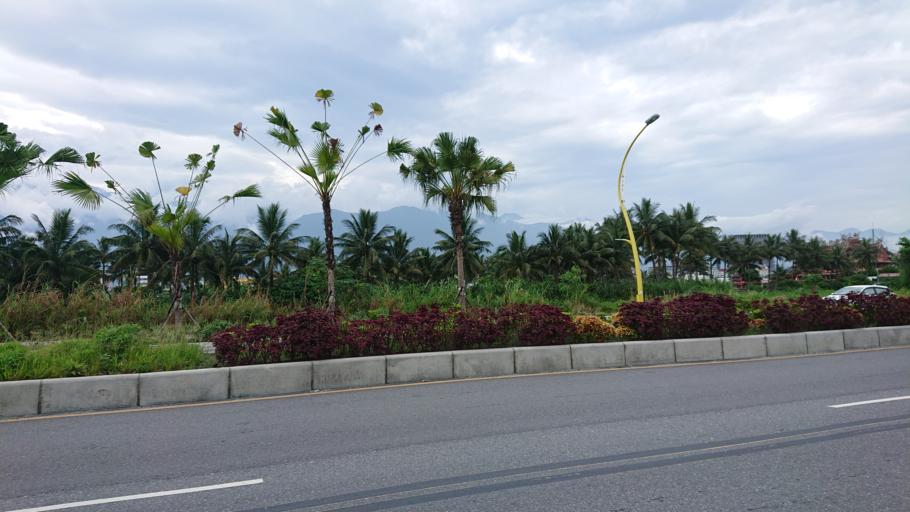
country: TW
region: Taiwan
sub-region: Hualien
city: Hualian
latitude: 23.9680
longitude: 121.6098
